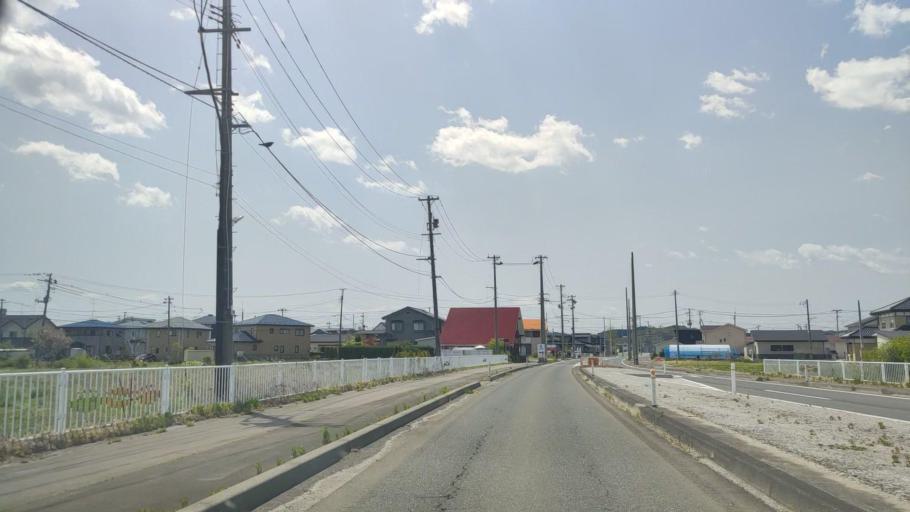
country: JP
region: Aomori
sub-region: Hachinohe Shi
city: Uchimaru
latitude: 40.5172
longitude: 141.4310
